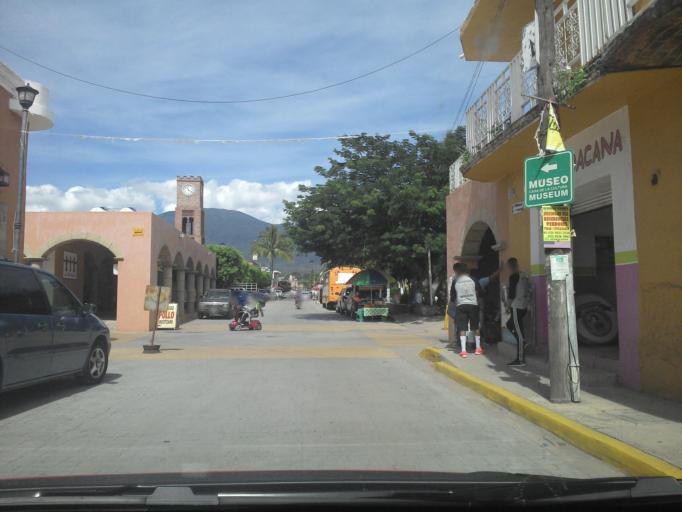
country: MX
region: Jalisco
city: Teuchitlan
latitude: 20.6833
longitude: -103.8478
